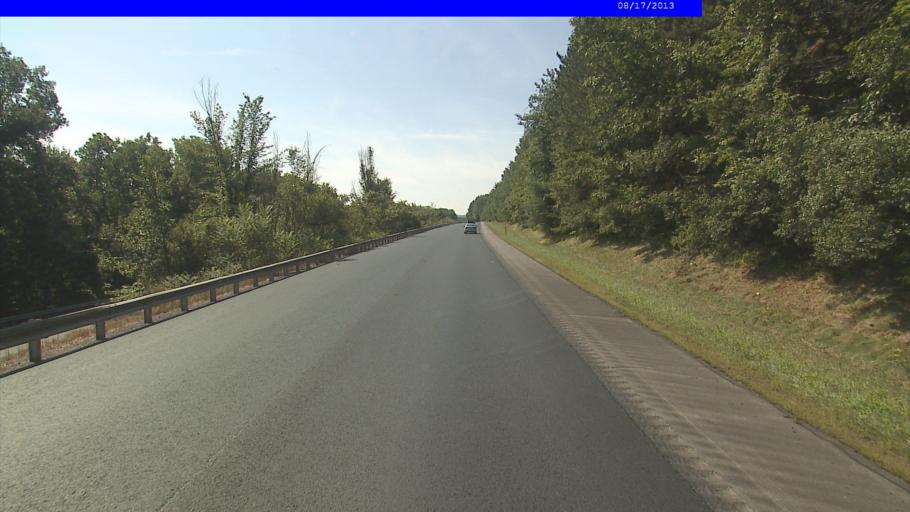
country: US
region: New Hampshire
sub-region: Cheshire County
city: Chesterfield
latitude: 42.9334
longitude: -72.5281
